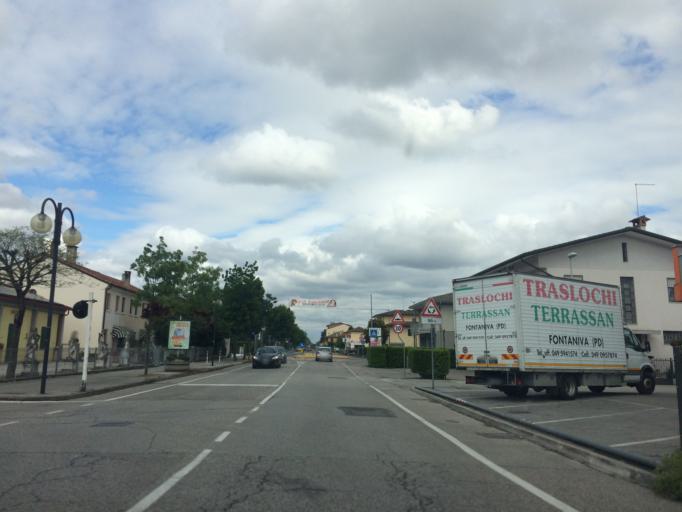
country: IT
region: Veneto
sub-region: Provincia di Padova
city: Cittadella
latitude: 45.6497
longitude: 11.7909
